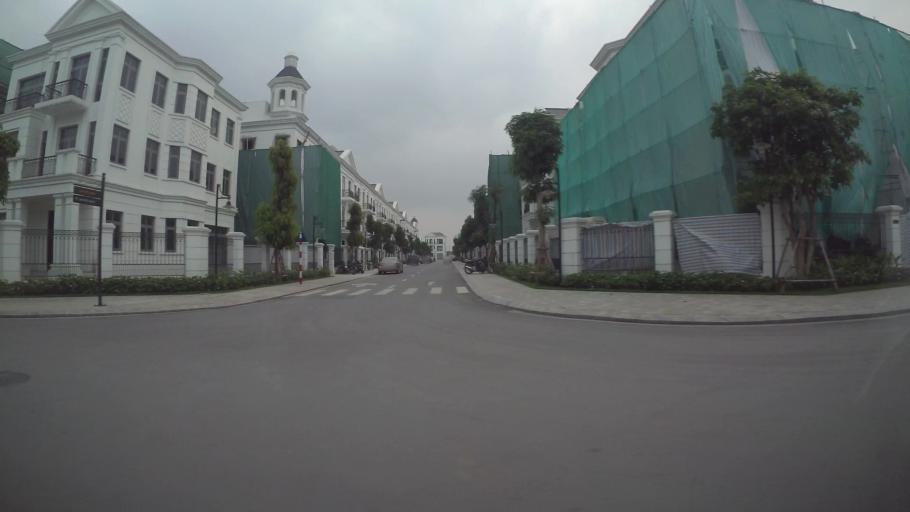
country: VN
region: Ha Noi
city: Trau Quy
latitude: 21.0501
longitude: 105.9036
